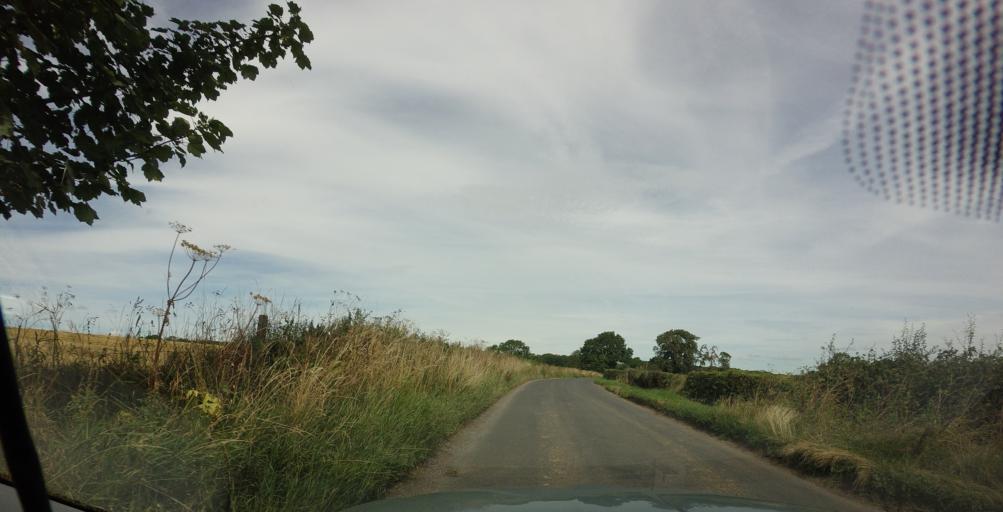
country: GB
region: England
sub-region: North Yorkshire
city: Ripon
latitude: 54.0950
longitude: -1.5083
